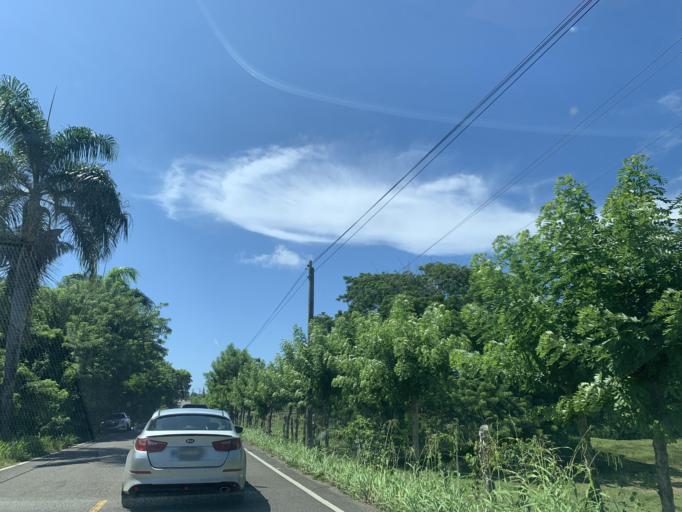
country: DO
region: Maria Trinidad Sanchez
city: Cabrera
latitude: 19.6676
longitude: -69.9492
